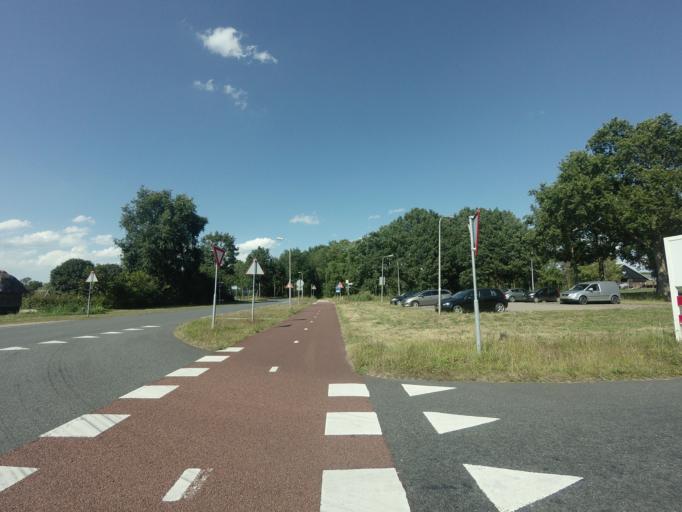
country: NL
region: Drenthe
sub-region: Gemeente Hoogeveen
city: Hoogeveen
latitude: 52.6083
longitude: 6.4581
